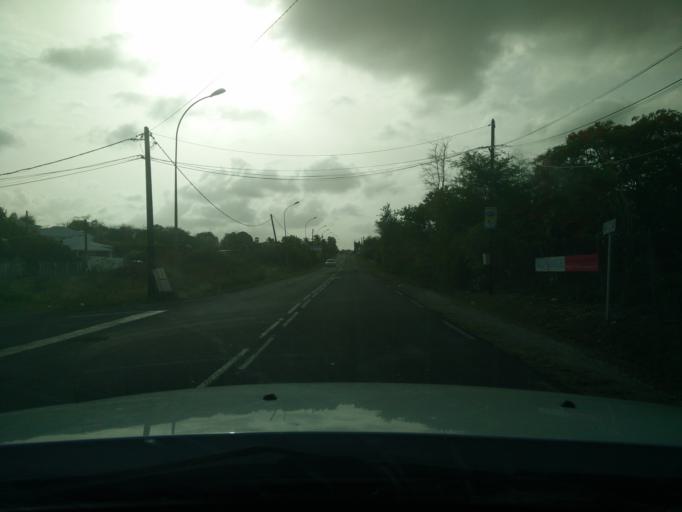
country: GP
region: Guadeloupe
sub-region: Guadeloupe
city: Saint-Francois
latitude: 16.2542
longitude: -61.2863
